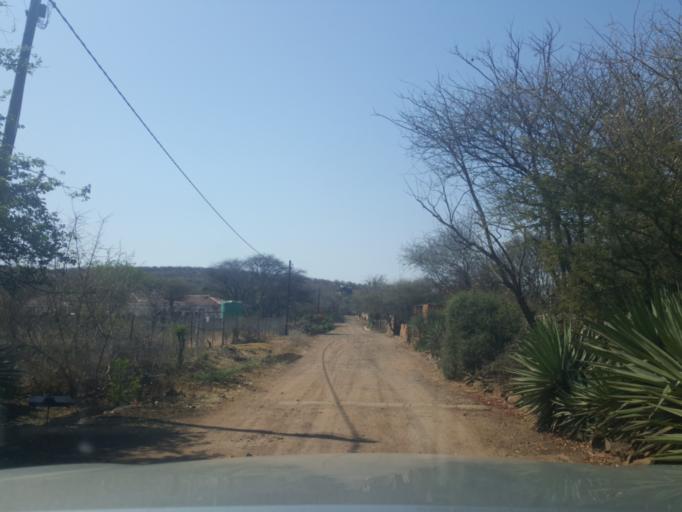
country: BW
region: Kweneng
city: Gabane
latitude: -24.7438
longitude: 25.8296
